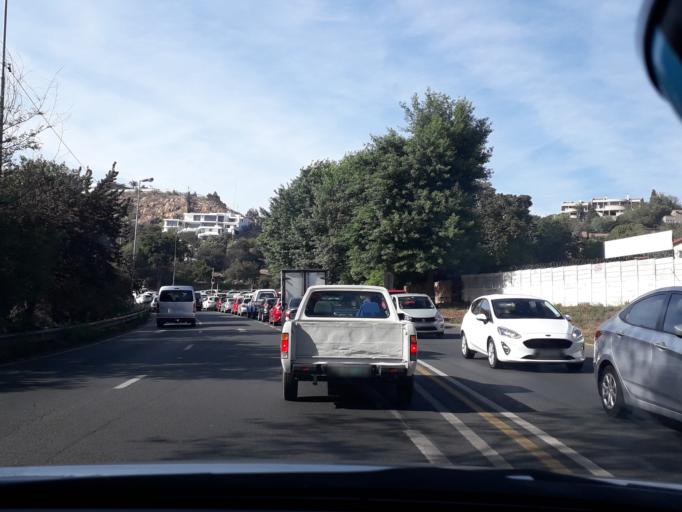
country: ZA
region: Gauteng
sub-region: City of Johannesburg Metropolitan Municipality
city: Roodepoort
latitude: -26.1381
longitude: 27.8932
